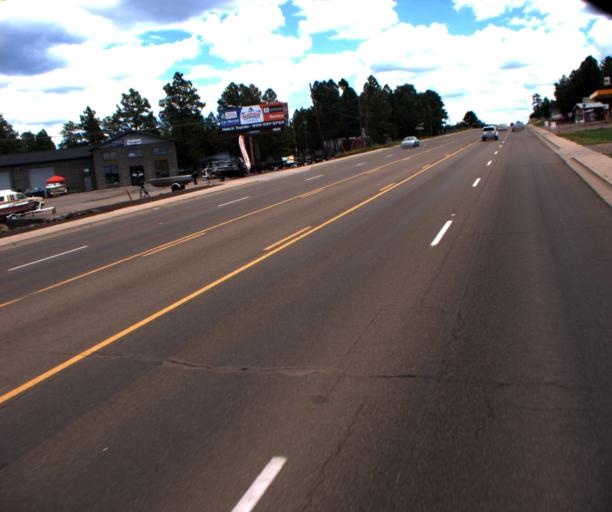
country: US
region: Arizona
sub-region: Navajo County
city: Lake of the Woods
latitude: 34.1667
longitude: -109.9947
